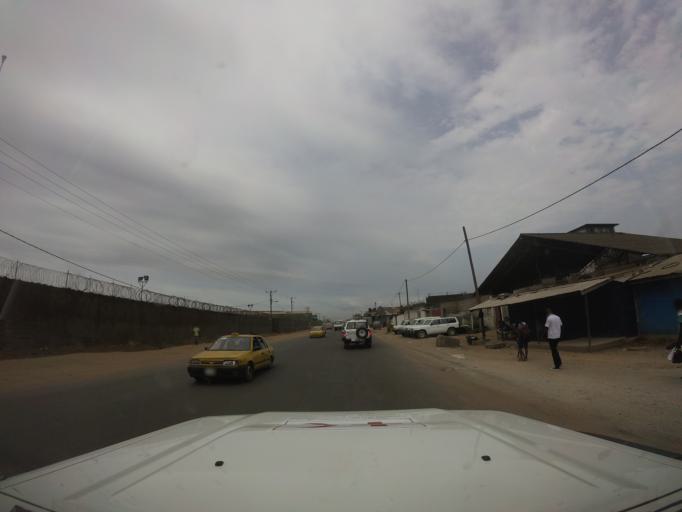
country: LR
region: Montserrado
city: Monrovia
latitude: 6.3411
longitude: -10.7916
